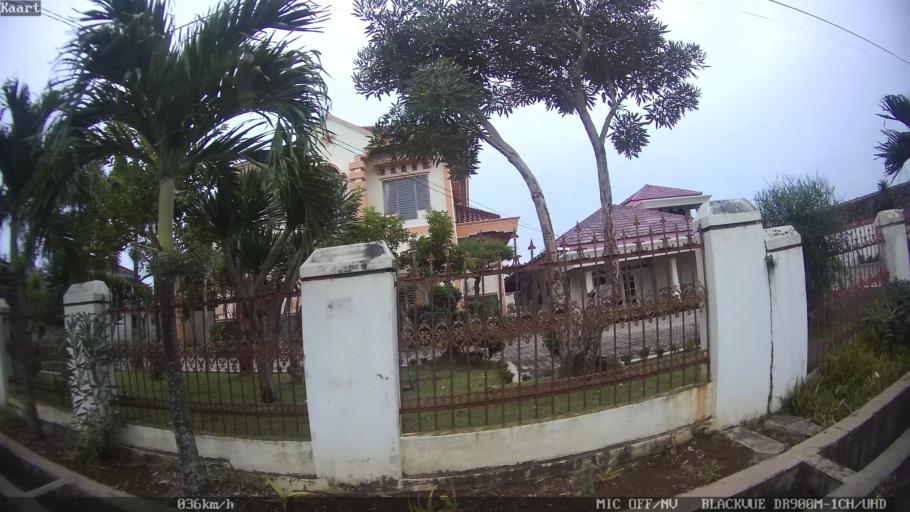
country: ID
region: Lampung
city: Kedaton
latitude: -5.3918
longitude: 105.2352
